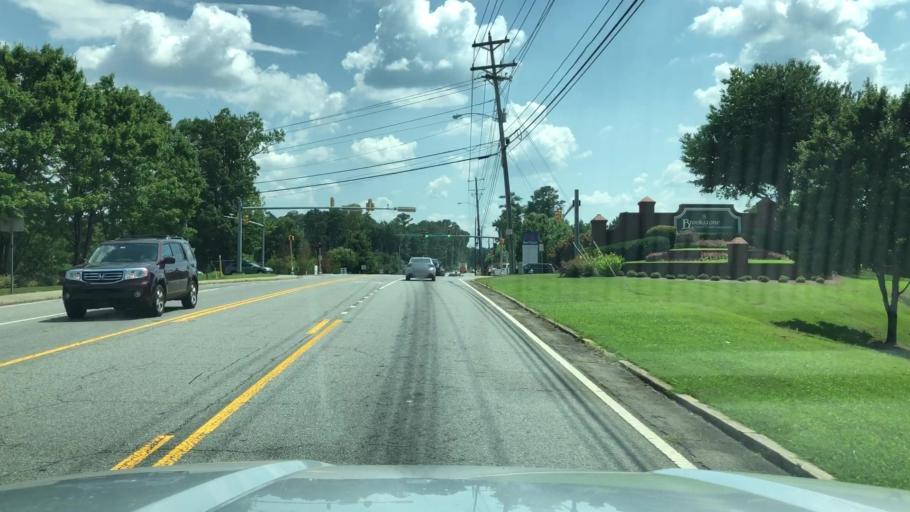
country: US
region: Georgia
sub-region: Cobb County
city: Acworth
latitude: 33.9982
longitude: -84.7052
